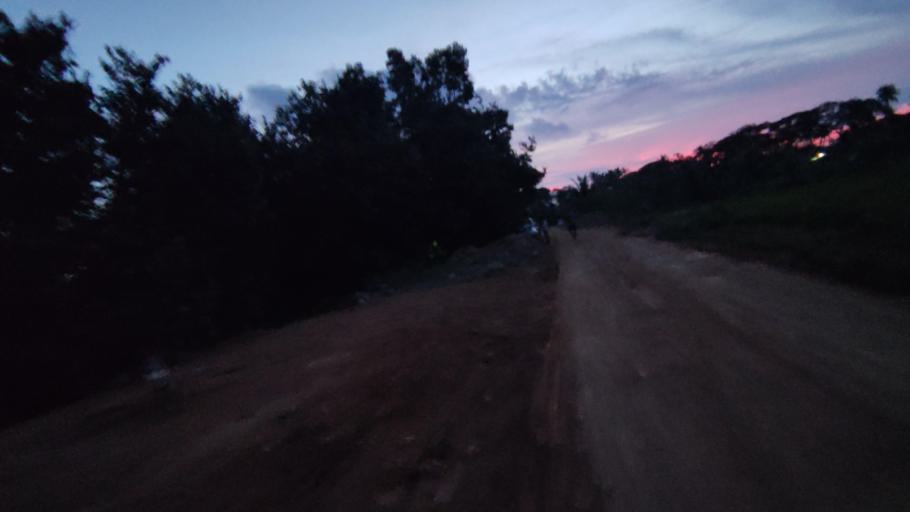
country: IN
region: Kerala
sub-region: Alappuzha
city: Shertallai
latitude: 9.6416
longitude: 76.4317
